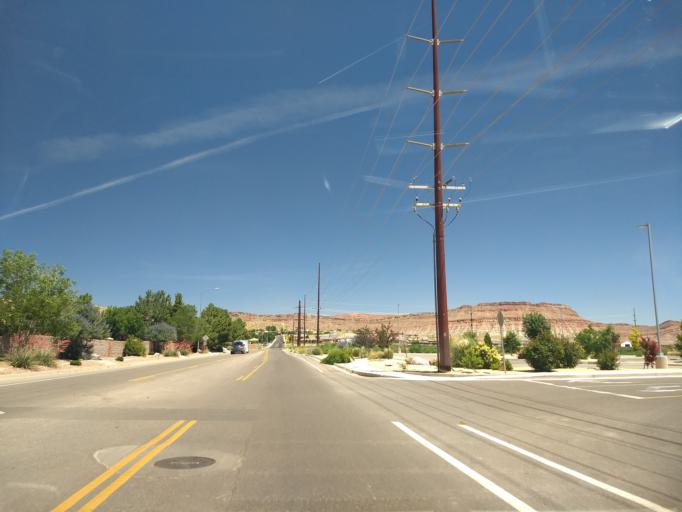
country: US
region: Utah
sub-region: Washington County
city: Washington
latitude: 37.0888
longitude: -113.5031
